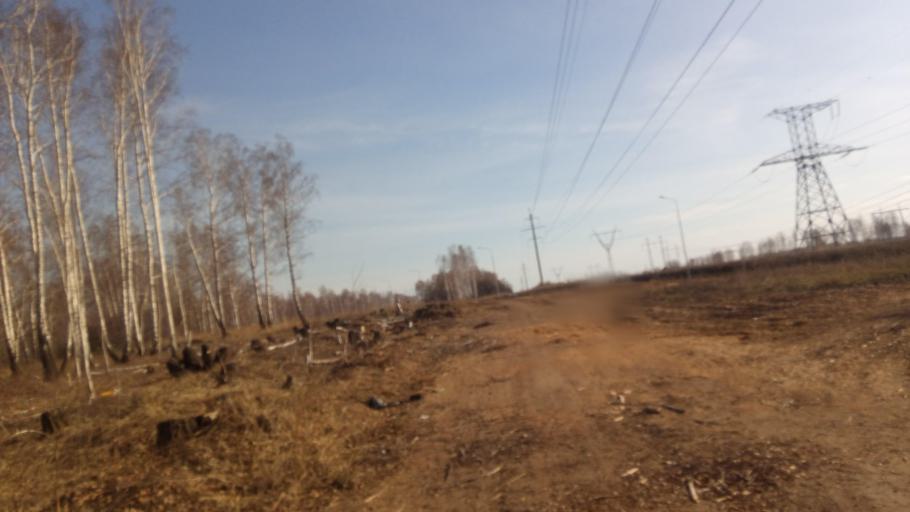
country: RU
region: Chelyabinsk
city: Sargazy
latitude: 55.1159
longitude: 61.2359
